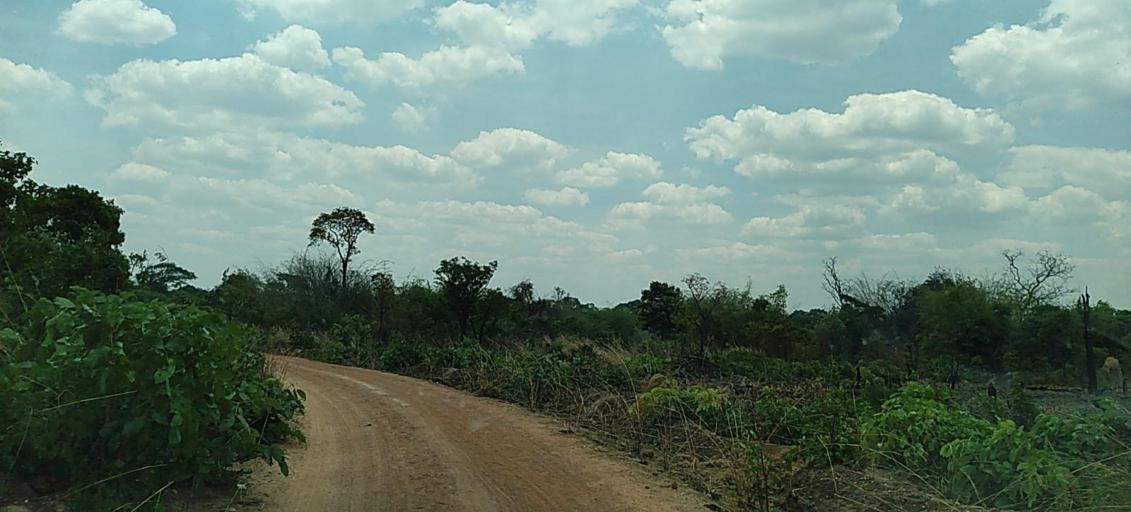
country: ZM
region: Copperbelt
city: Chililabombwe
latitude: -12.3896
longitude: 27.9193
